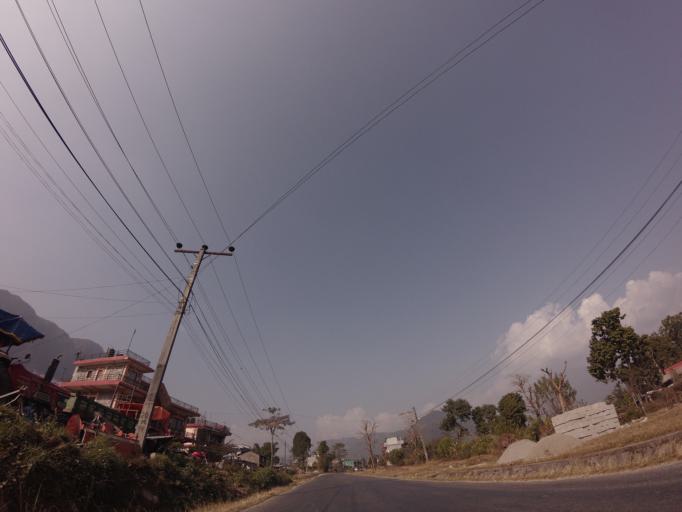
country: NP
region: Western Region
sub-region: Gandaki Zone
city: Pokhara
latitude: 28.2741
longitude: 83.9412
